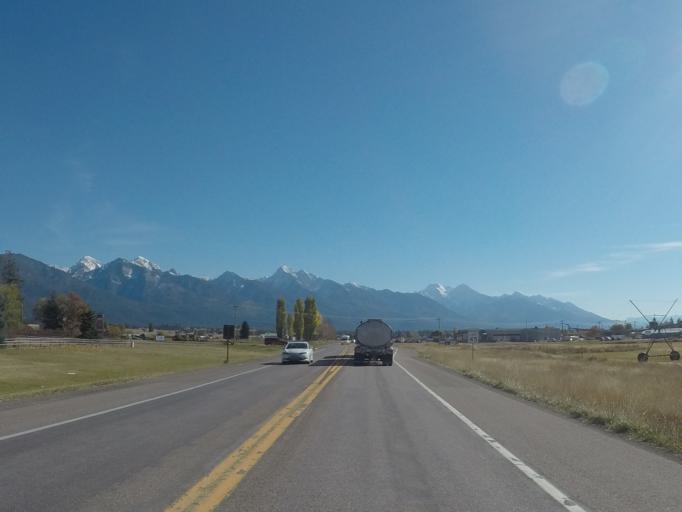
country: US
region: Montana
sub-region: Lake County
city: Ronan
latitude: 47.5390
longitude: -114.1043
